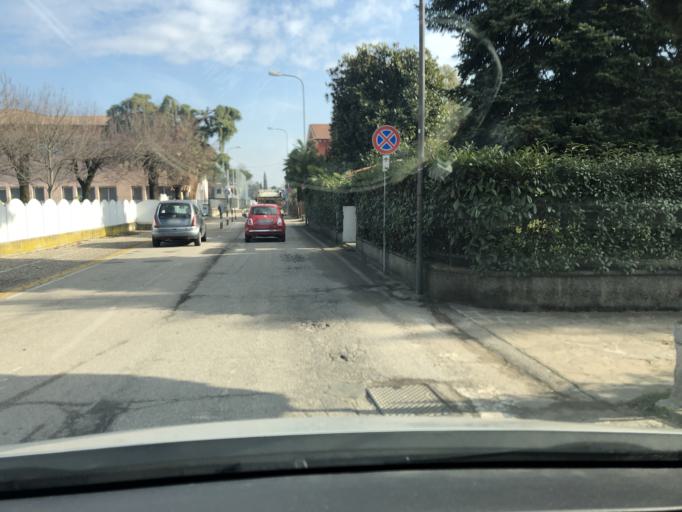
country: IT
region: Veneto
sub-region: Provincia di Verona
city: Lugagnano
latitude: 45.4308
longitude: 10.8874
